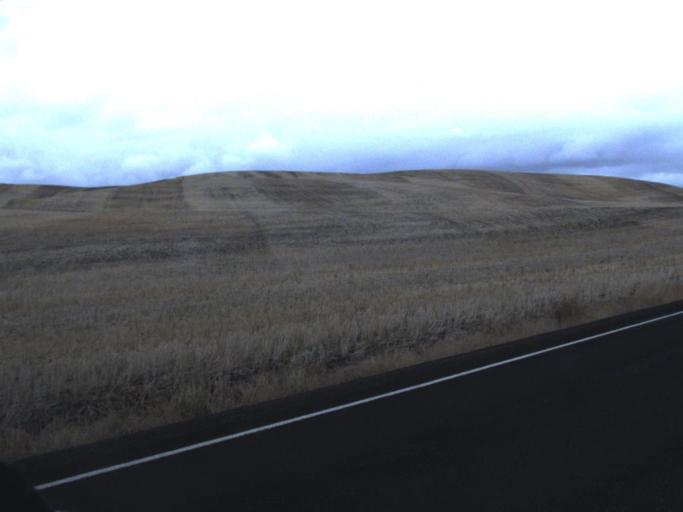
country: US
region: Washington
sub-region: Whitman County
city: Colfax
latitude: 47.1998
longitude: -117.3483
